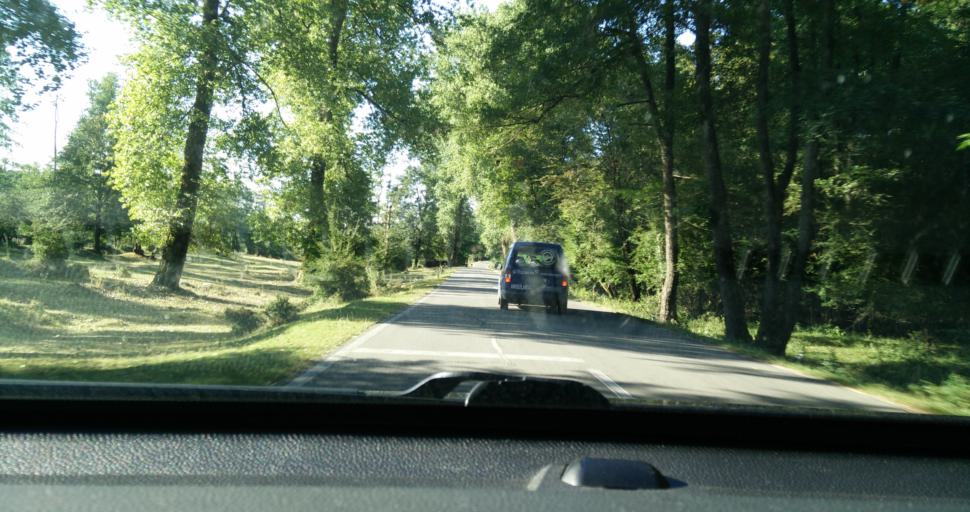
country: RO
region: Gorj
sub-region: Comuna Polovragi
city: Polovragi
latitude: 45.1766
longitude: 23.7843
